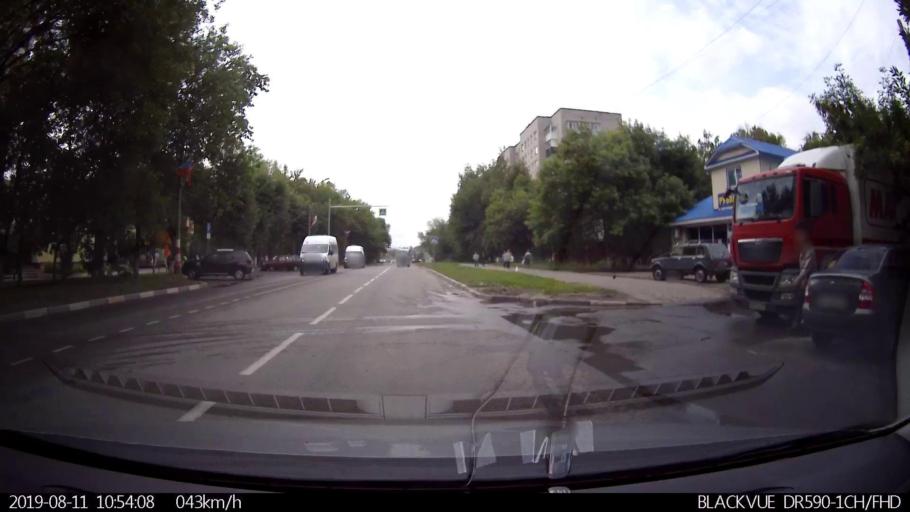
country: RU
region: Ulyanovsk
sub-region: Ulyanovskiy Rayon
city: Ulyanovsk
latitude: 54.2579
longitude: 48.3342
